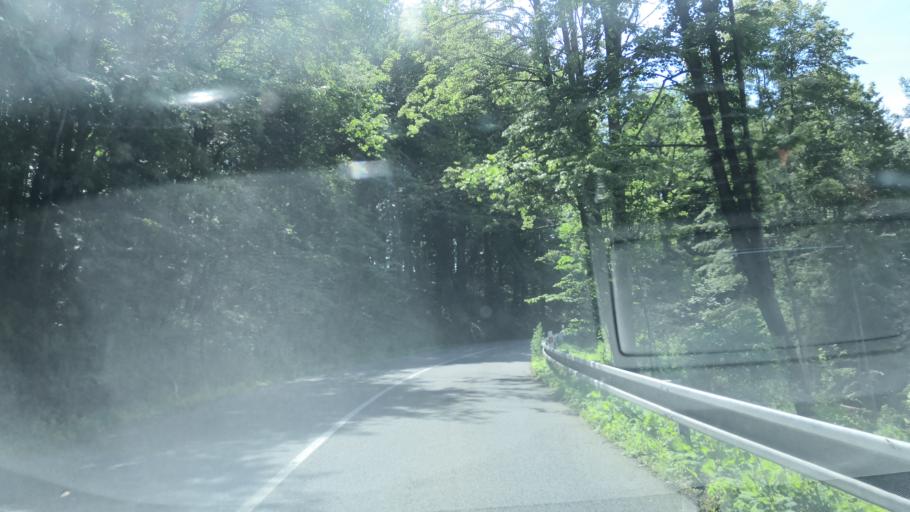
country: CZ
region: Zlin
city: Valasska Bystrice
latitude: 49.4295
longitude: 18.1284
